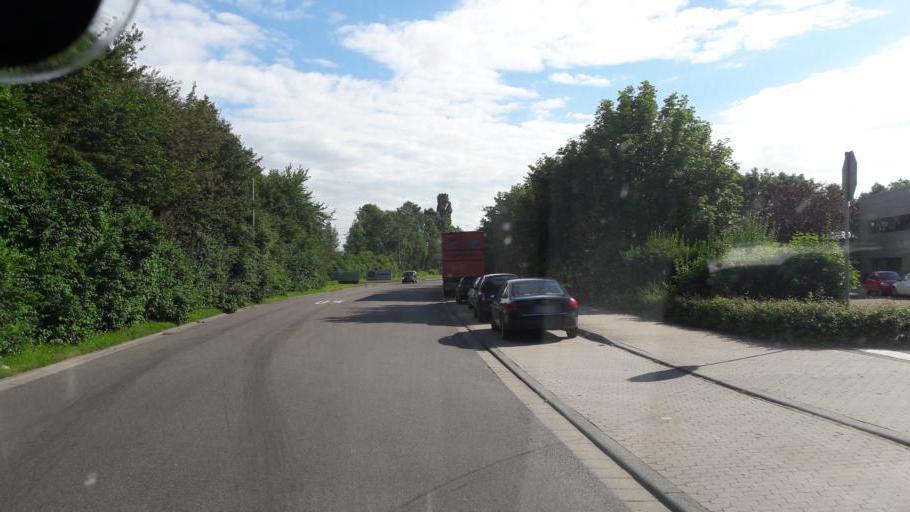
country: DE
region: Baden-Wuerttemberg
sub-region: Karlsruhe Region
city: Karlsdorf-Neuthard
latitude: 49.1283
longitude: 8.5627
